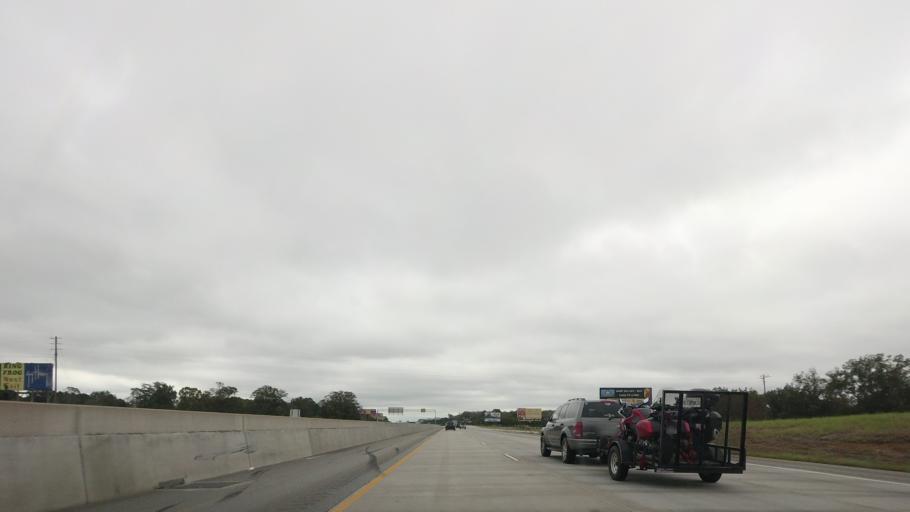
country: US
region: Georgia
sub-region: Cook County
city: Sparks
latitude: 31.1645
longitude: -83.4491
